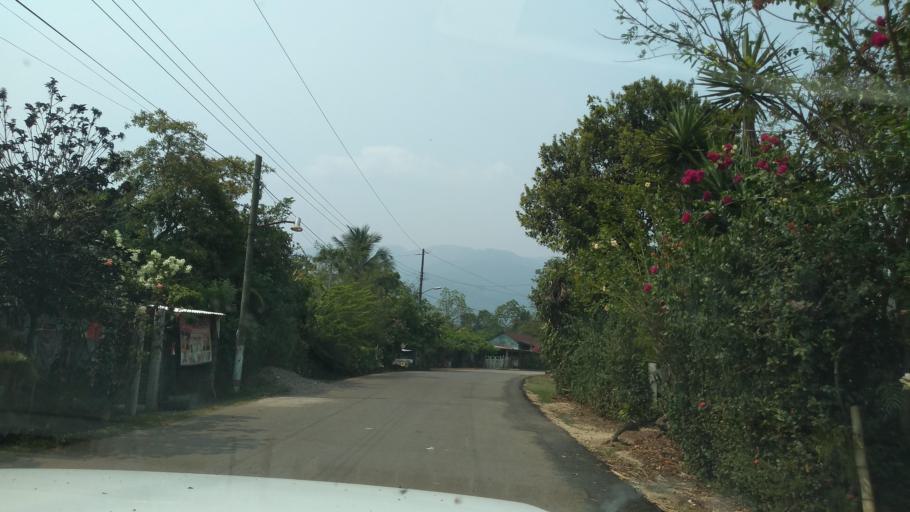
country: MX
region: Veracruz
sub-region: Tezonapa
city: Laguna Chica (Pueblo Nuevo)
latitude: 18.5414
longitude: -96.7809
